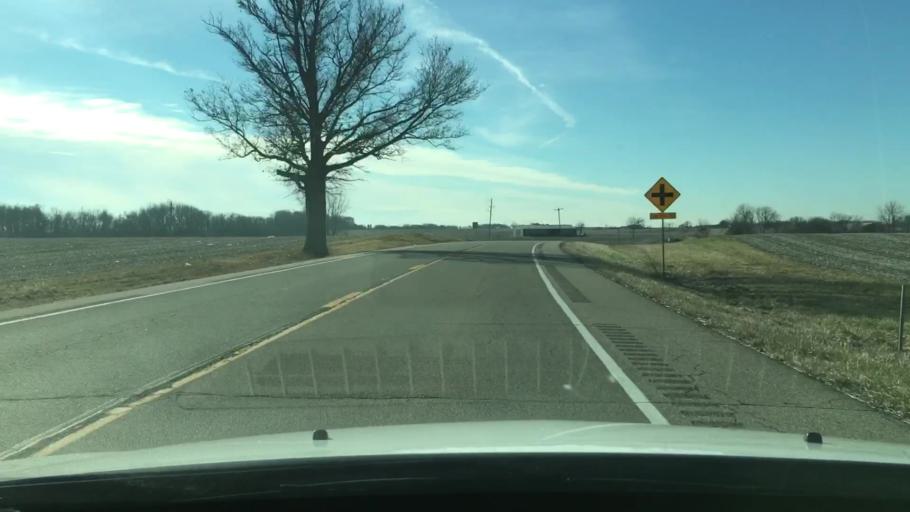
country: US
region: Illinois
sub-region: Woodford County
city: Washburn
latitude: 40.8741
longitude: -89.3194
